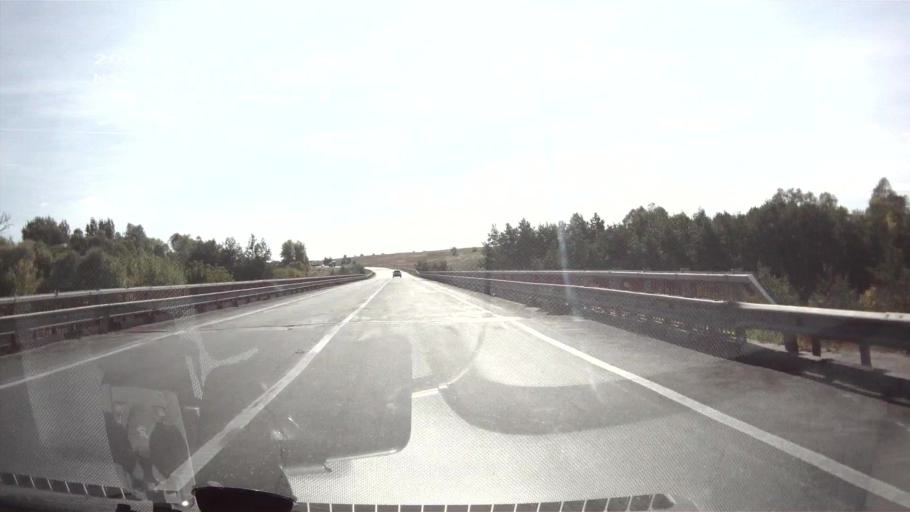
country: RU
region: Samara
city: Varlamovo
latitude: 53.1327
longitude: 48.2872
